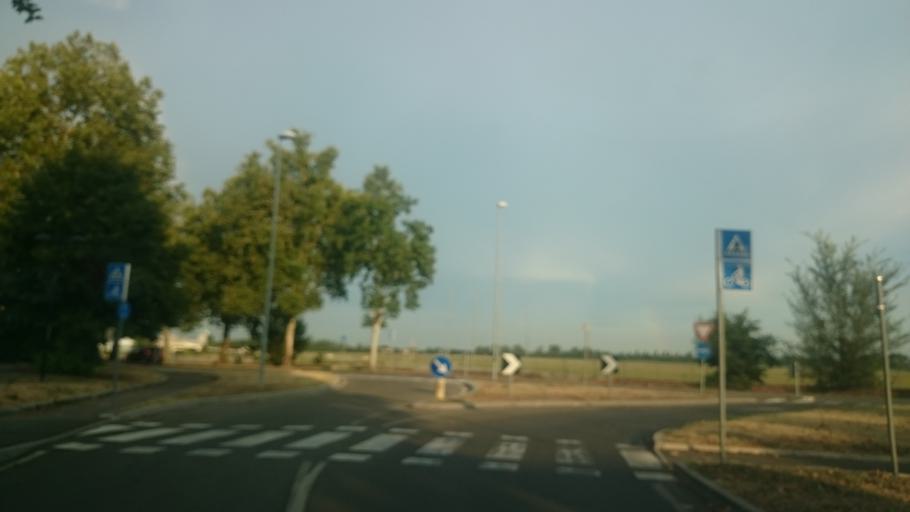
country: IT
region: Emilia-Romagna
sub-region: Provincia di Reggio Emilia
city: Reggio nell'Emilia
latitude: 44.7020
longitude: 10.6584
